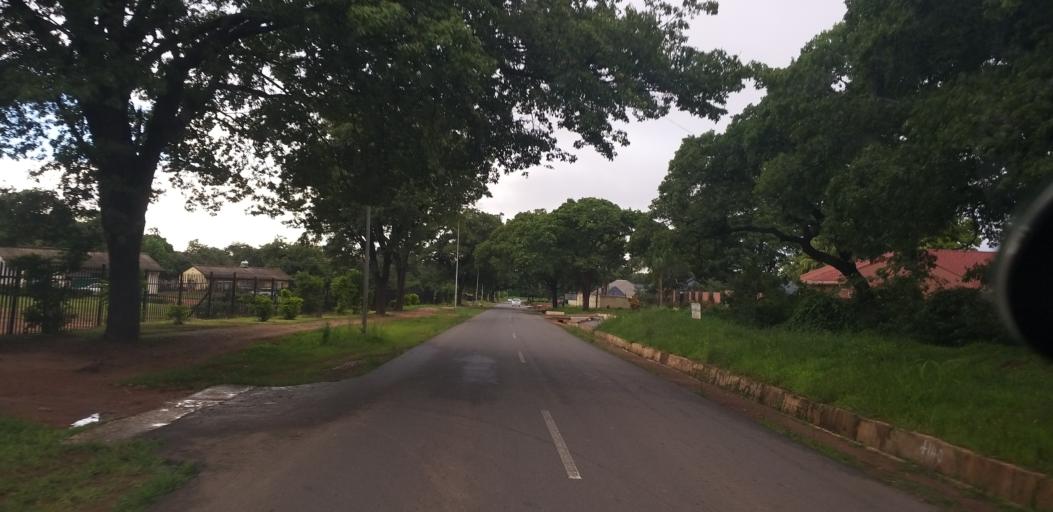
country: ZM
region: Lusaka
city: Lusaka
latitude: -15.4316
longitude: 28.3317
